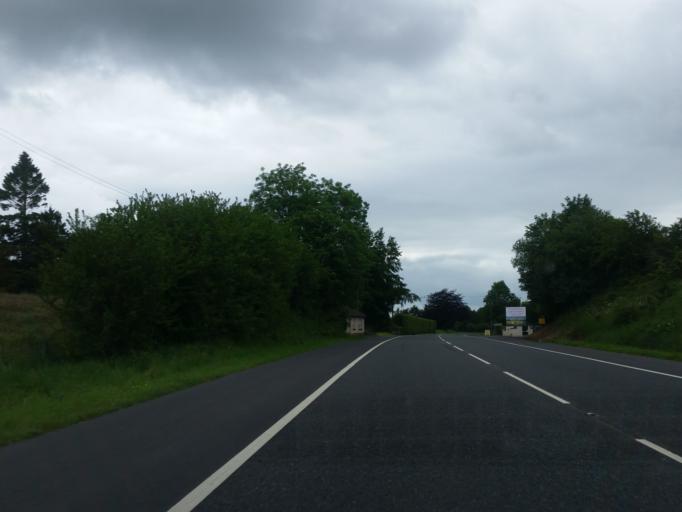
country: GB
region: Northern Ireland
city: Fivemiletown
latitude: 54.3679
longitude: -7.3366
